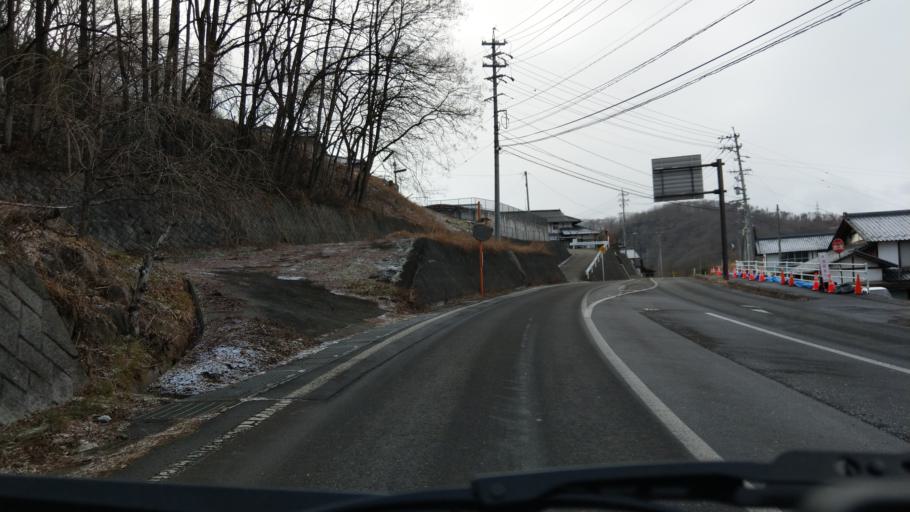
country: JP
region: Nagano
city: Kamimaruko
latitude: 36.3257
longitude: 138.3456
